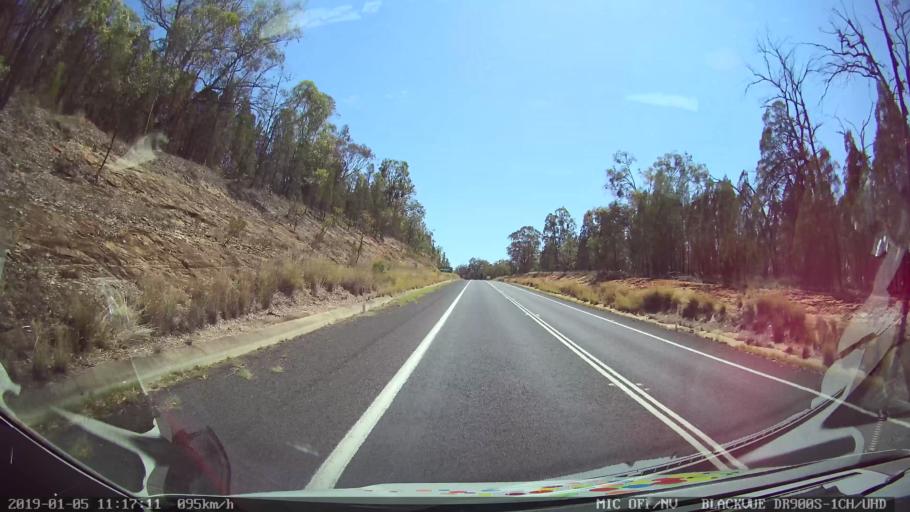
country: AU
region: New South Wales
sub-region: Warrumbungle Shire
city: Coonabarabran
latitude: -31.3292
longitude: 149.3044
